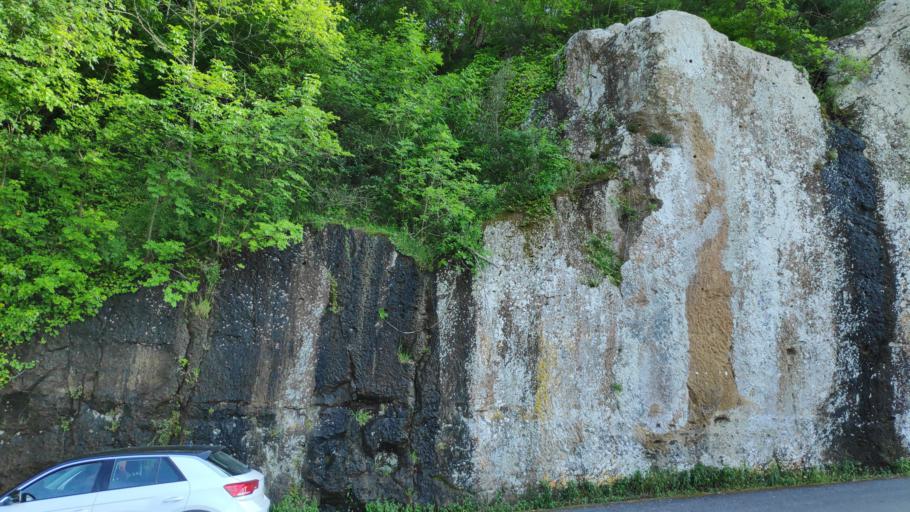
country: IT
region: Tuscany
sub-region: Provincia di Grosseto
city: Pitigliano
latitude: 42.6308
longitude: 11.6643
